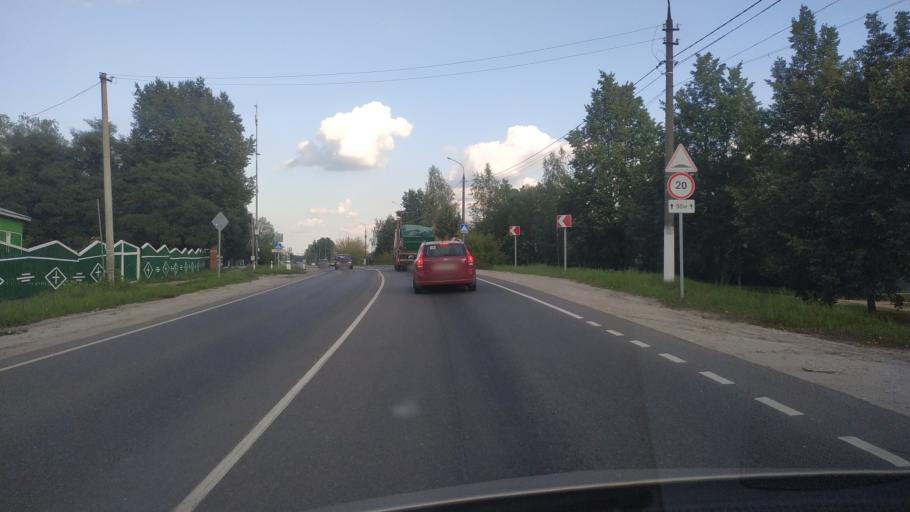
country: RU
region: Moskovskaya
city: Shatura
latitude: 55.5781
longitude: 39.4866
